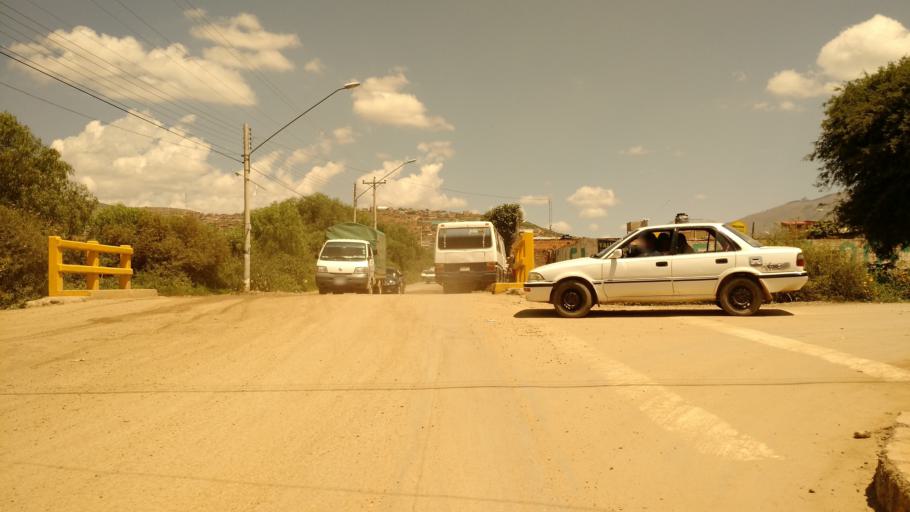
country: BO
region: Cochabamba
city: Cochabamba
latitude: -17.4542
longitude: -66.1562
